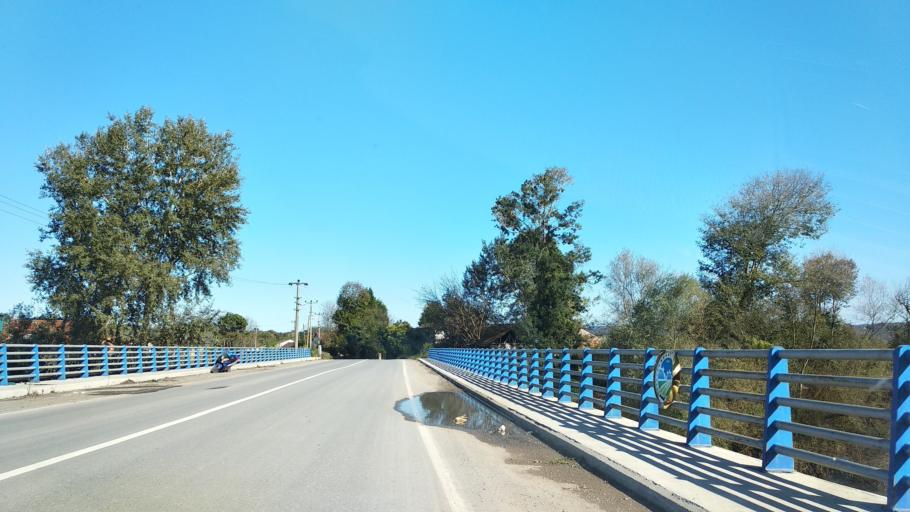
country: TR
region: Sakarya
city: Ortakoy
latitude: 41.0248
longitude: 30.6020
